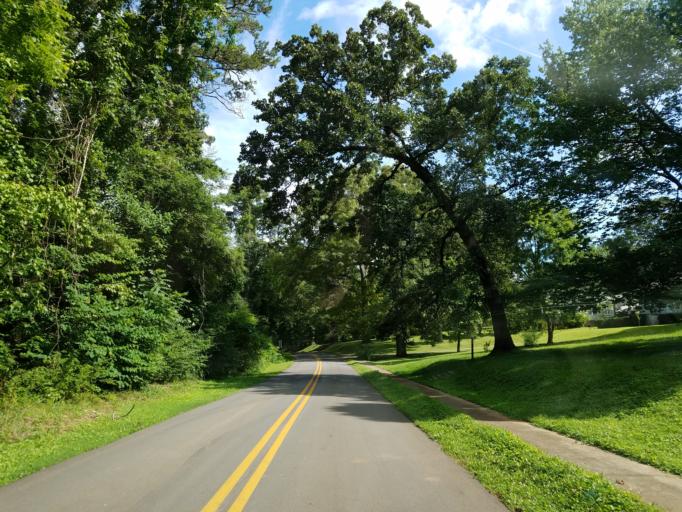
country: US
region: Georgia
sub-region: Pickens County
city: Nelson
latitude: 34.4185
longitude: -84.3897
